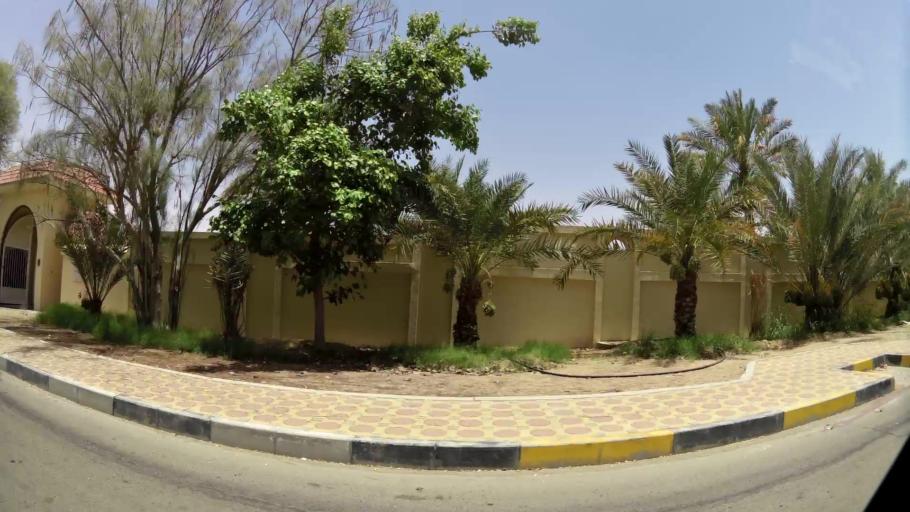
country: OM
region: Al Buraimi
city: Al Buraymi
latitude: 24.2654
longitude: 55.7264
